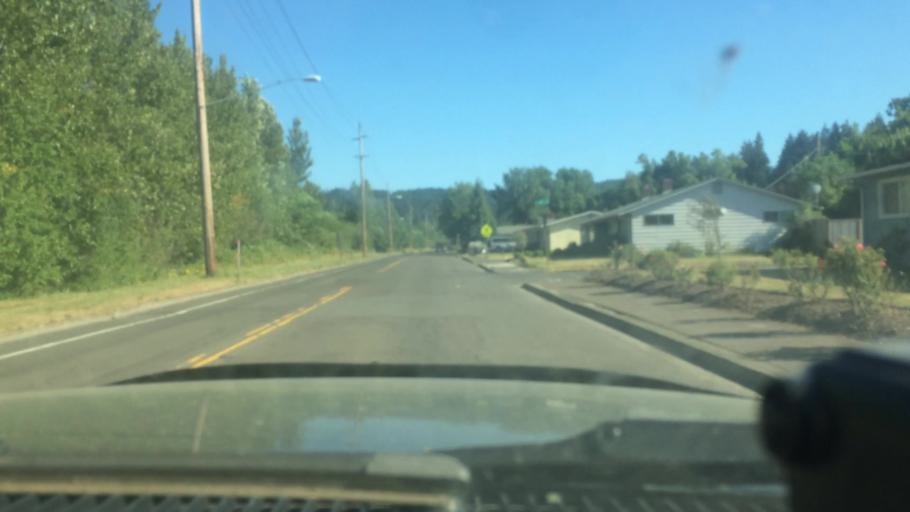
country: US
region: Oregon
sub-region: Lane County
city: Eugene
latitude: 44.0146
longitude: -123.0784
